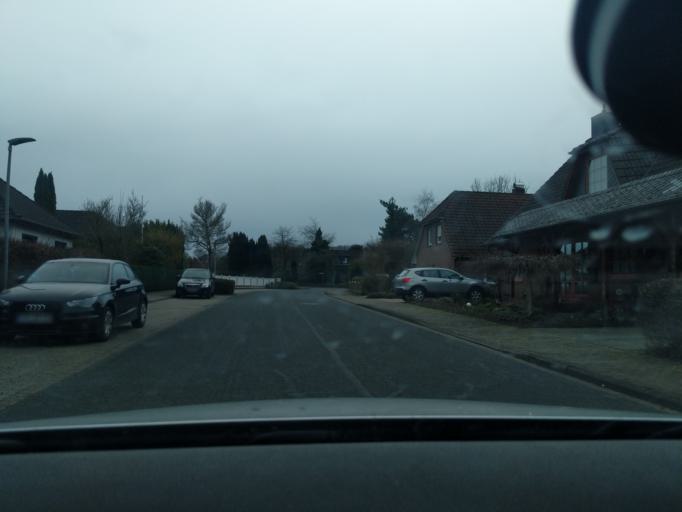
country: DE
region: Lower Saxony
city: Bremervorde
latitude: 53.4643
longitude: 9.1980
